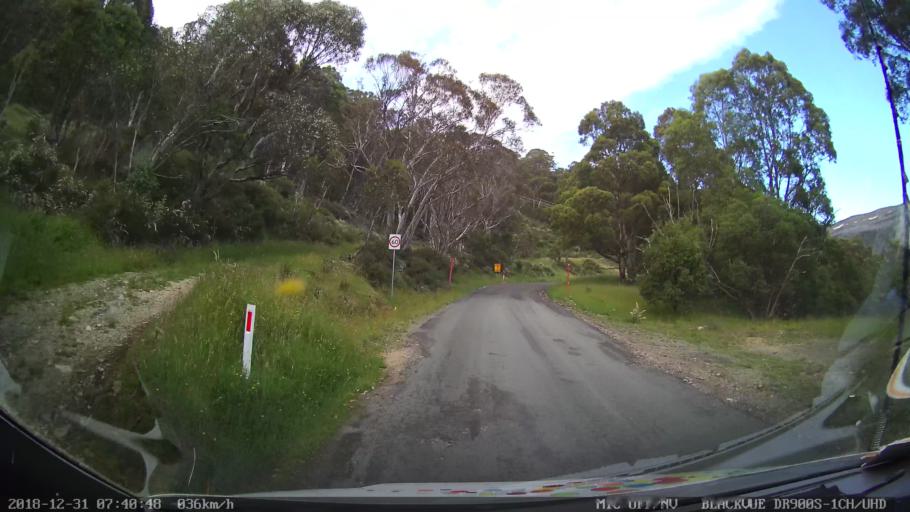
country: AU
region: New South Wales
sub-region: Snowy River
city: Jindabyne
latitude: -36.3523
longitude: 148.4156
